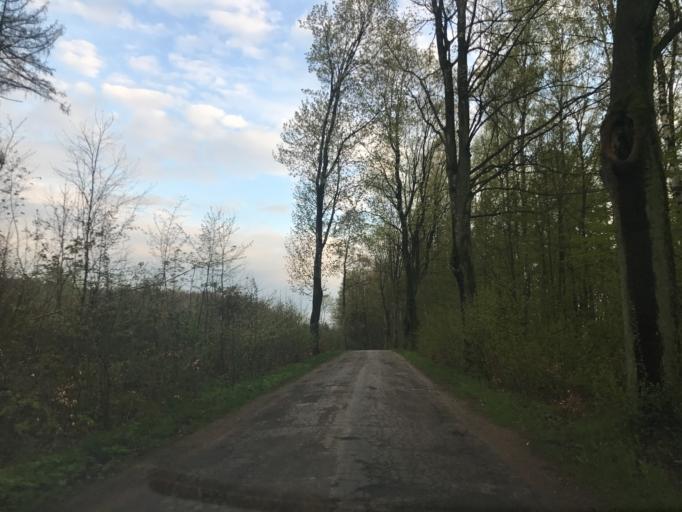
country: PL
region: Warmian-Masurian Voivodeship
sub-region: Powiat ilawski
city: Lubawa
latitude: 53.5543
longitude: 19.8968
